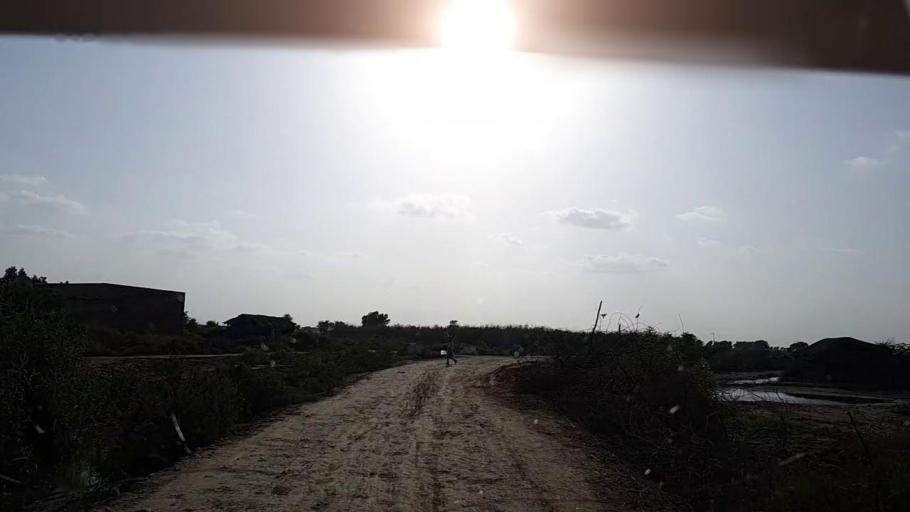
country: PK
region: Sindh
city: Badin
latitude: 24.5592
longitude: 68.8988
